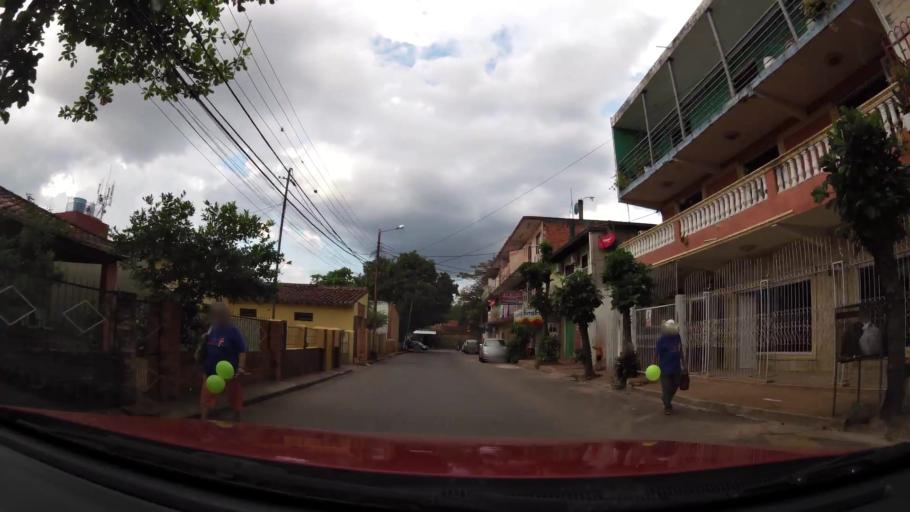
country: PY
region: Central
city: Fernando de la Mora
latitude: -25.3375
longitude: -57.5459
